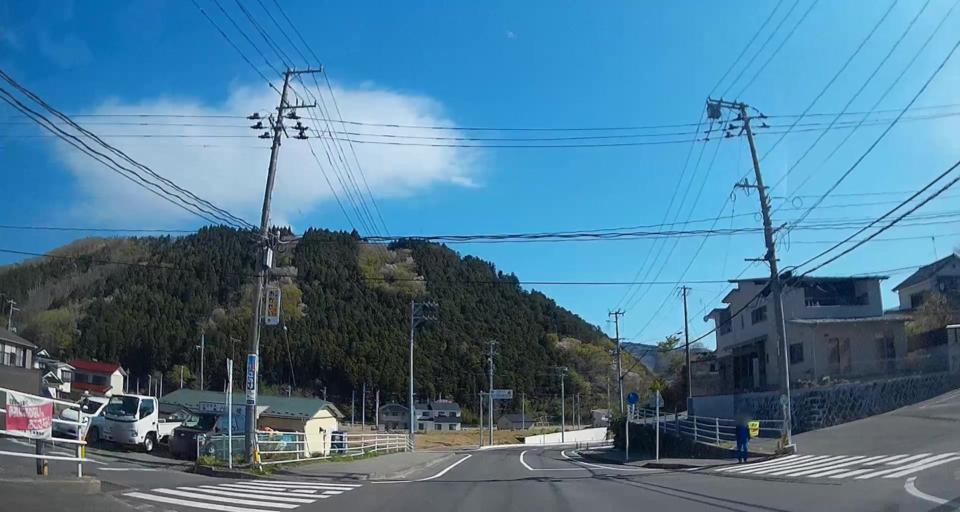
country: JP
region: Miyagi
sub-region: Oshika Gun
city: Onagawa Cho
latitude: 38.4384
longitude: 141.4390
